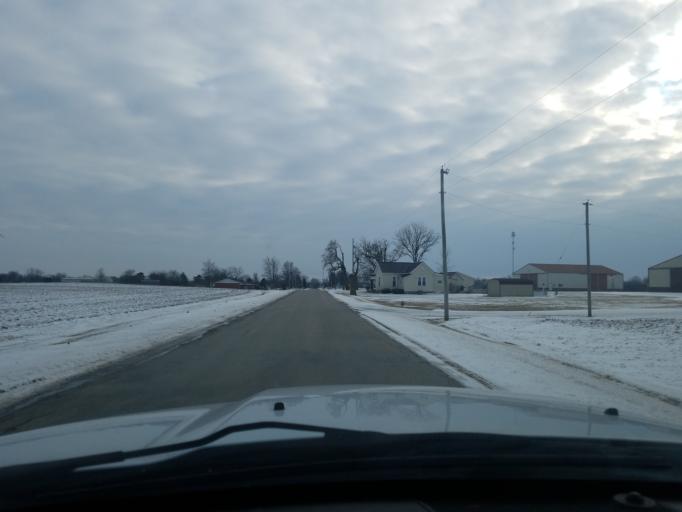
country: US
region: Indiana
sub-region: Randolph County
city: Winchester
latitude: 40.1954
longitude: -84.9797
